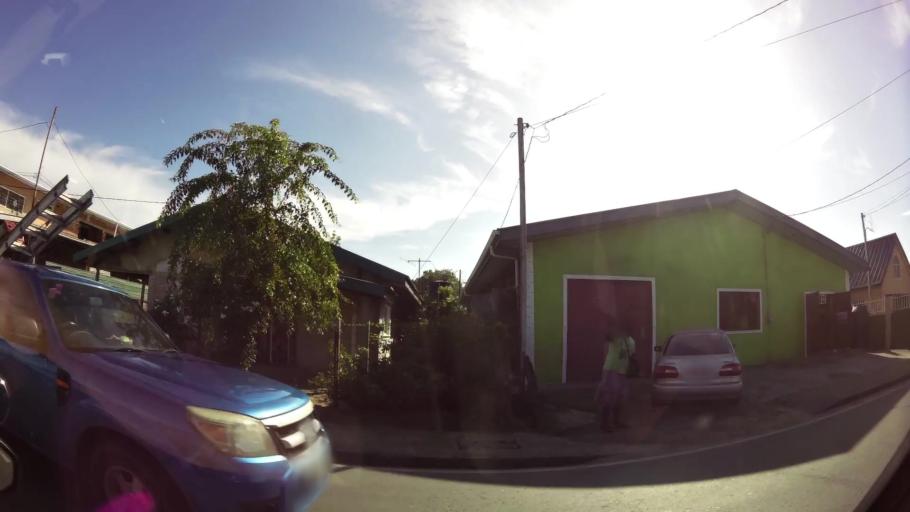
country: TT
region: Chaguanas
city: Chaguanas
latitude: 10.5201
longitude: -61.3789
